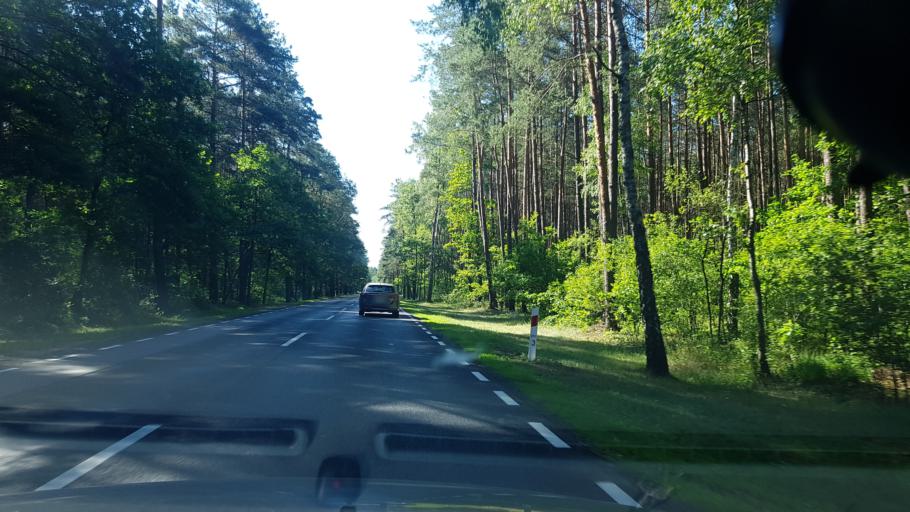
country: PL
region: Masovian Voivodeship
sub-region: Powiat wyszkowski
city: Branszczyk
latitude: 52.5746
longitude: 21.5389
